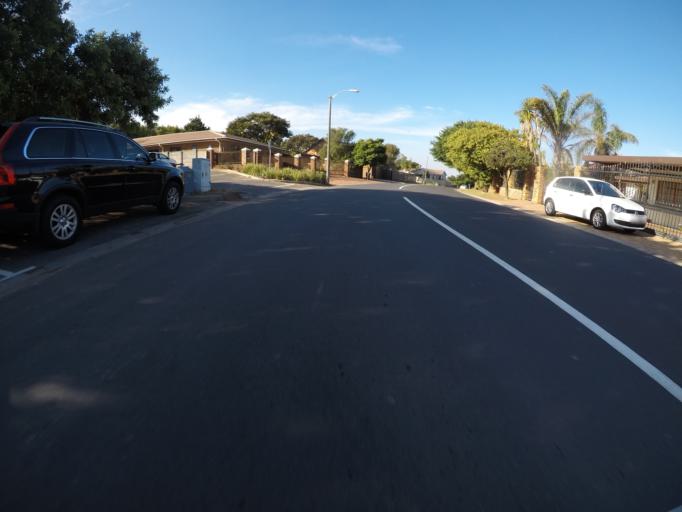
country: ZA
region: Western Cape
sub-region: City of Cape Town
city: Kraaifontein
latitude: -33.8746
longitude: 18.6454
